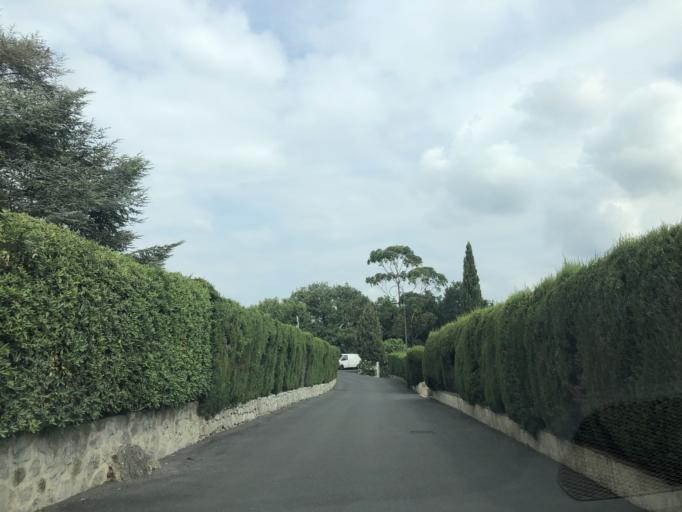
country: FR
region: Provence-Alpes-Cote d'Azur
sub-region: Departement des Alpes-Maritimes
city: Biot
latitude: 43.6253
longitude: 7.0846
